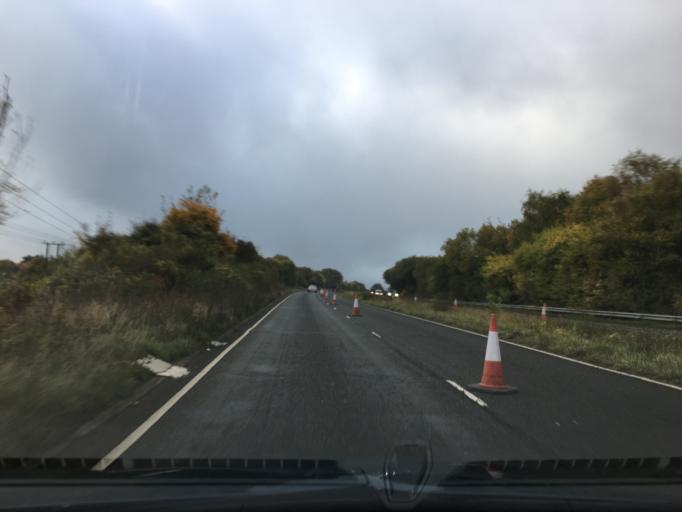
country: GB
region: England
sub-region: Hampshire
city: Alton
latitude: 51.1457
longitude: -0.9593
